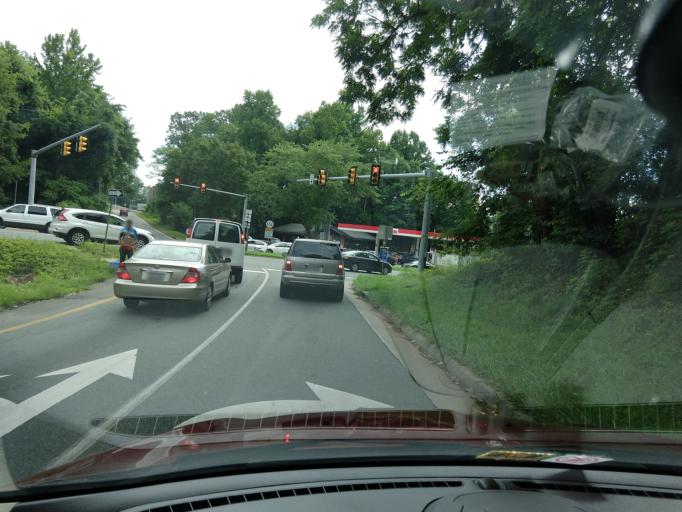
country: US
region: Virginia
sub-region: City of Charlottesville
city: Charlottesville
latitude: 38.0564
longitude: -78.5036
